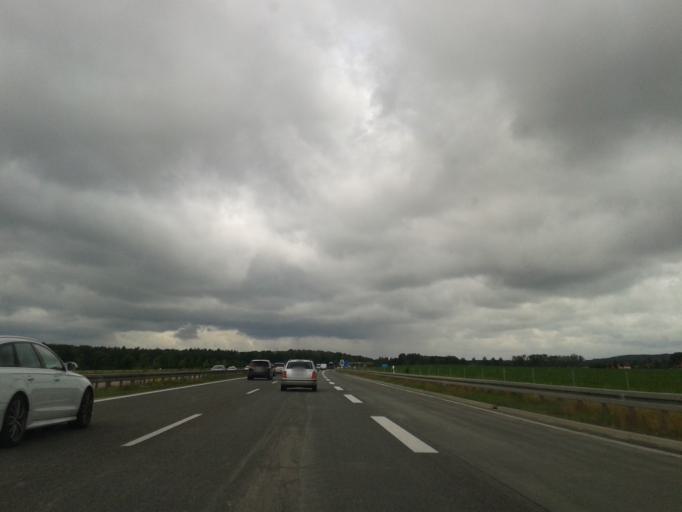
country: DE
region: Saxony
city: Naunhof
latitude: 51.2873
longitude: 12.6372
